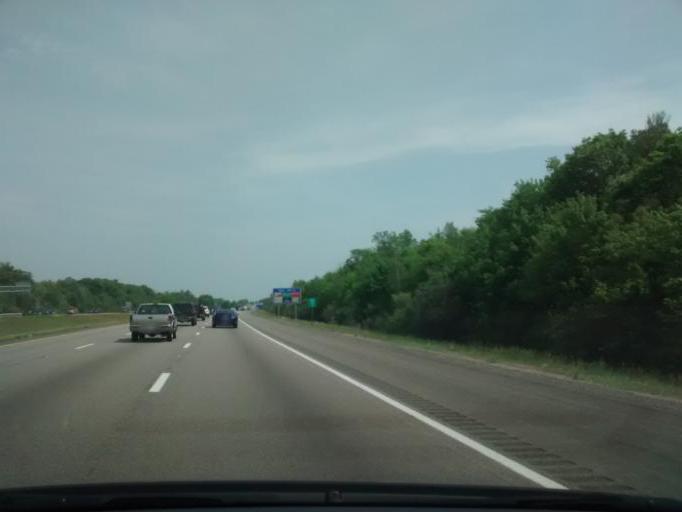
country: US
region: Massachusetts
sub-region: Bristol County
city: Mansfield Center
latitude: 42.0214
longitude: -71.2467
